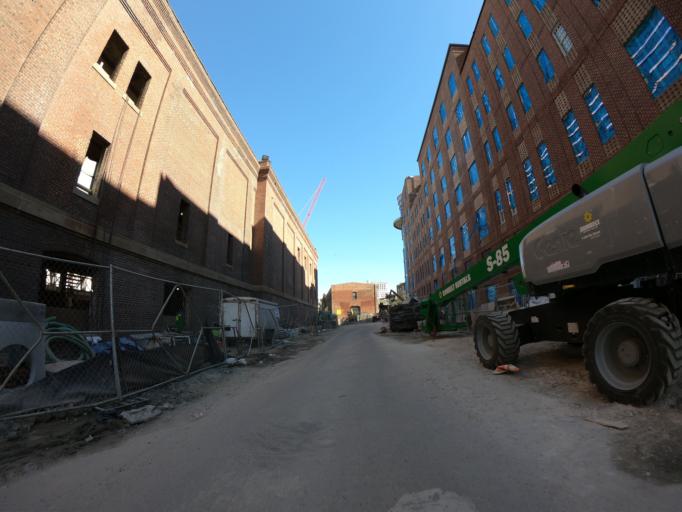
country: US
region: Georgia
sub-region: Chatham County
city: Savannah
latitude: 32.0834
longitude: -81.0959
